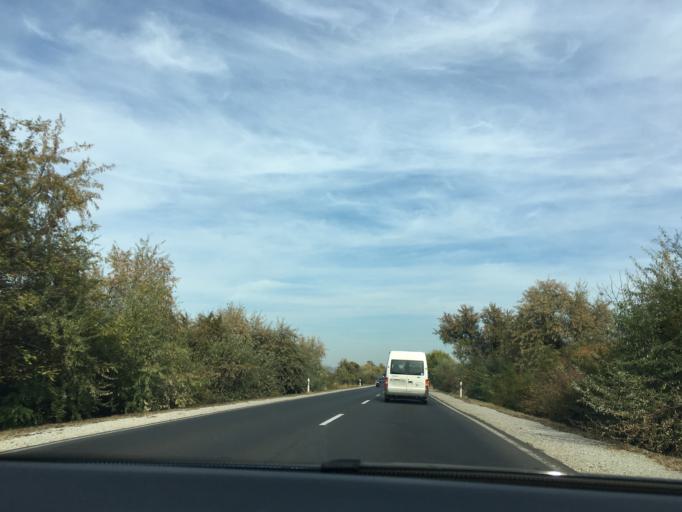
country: HU
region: Szabolcs-Szatmar-Bereg
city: Ujfeherto
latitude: 47.7867
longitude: 21.6923
